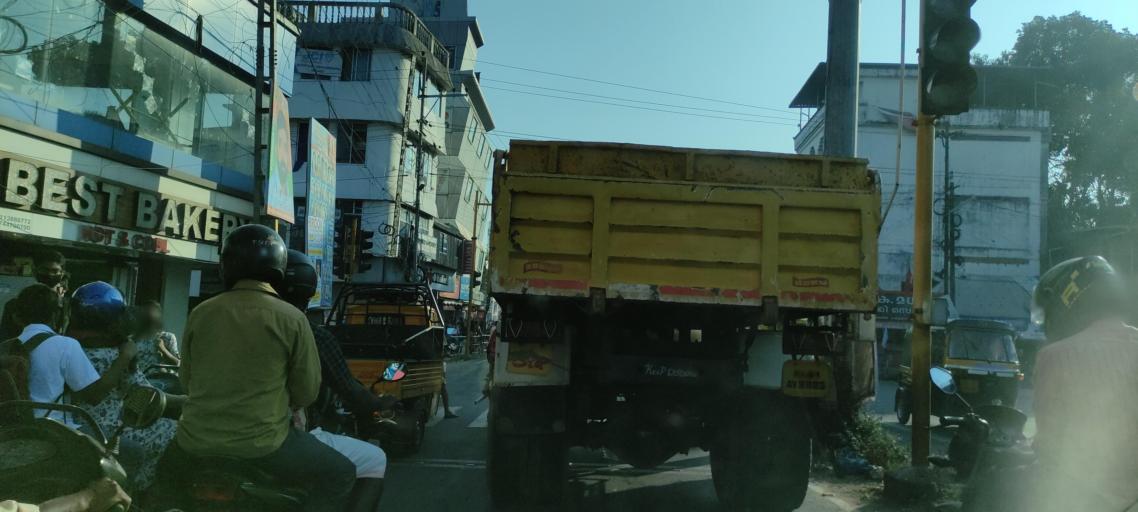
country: IN
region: Kerala
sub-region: Alappuzha
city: Kattanam
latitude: 9.1736
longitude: 76.6078
